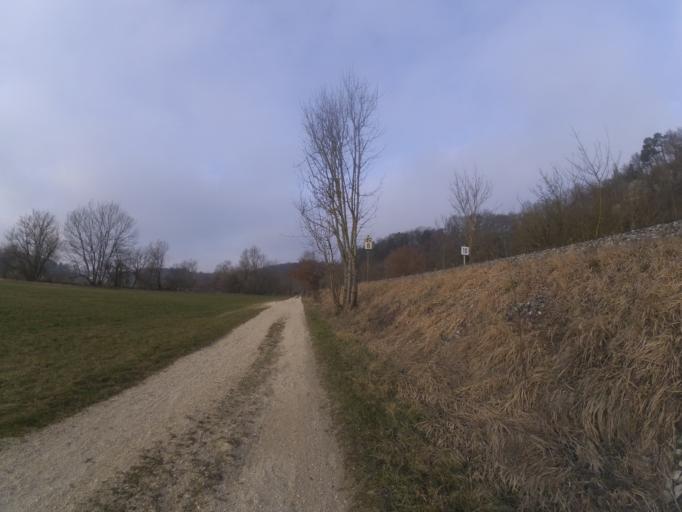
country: DE
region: Baden-Wuerttemberg
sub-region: Tuebingen Region
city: Lauterach
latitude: 48.2442
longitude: 9.5854
